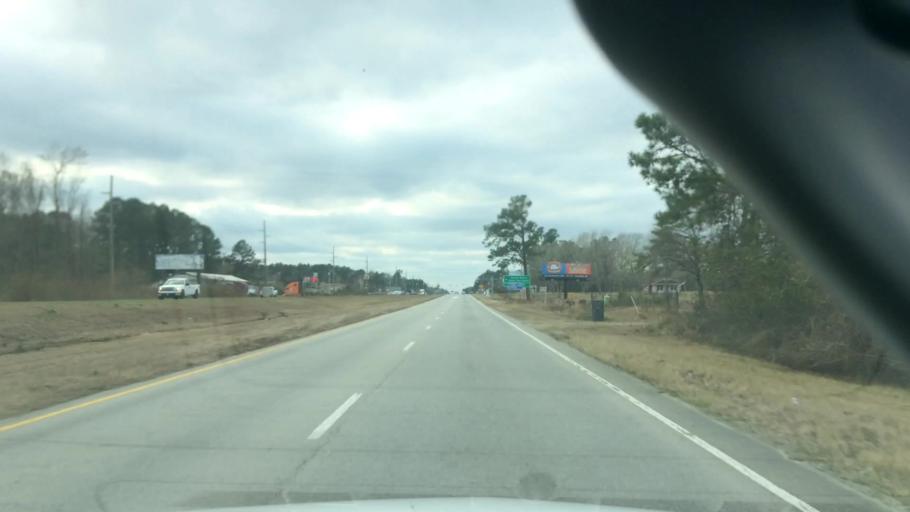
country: US
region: North Carolina
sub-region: Brunswick County
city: Sunset Beach
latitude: 33.9474
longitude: -78.4972
